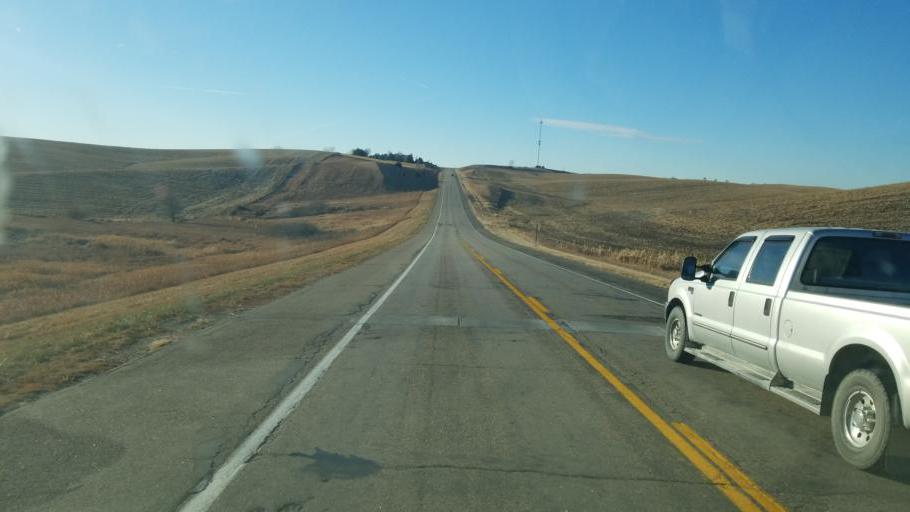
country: US
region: Nebraska
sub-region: Dixon County
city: Ponca
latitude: 42.4744
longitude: -96.7487
